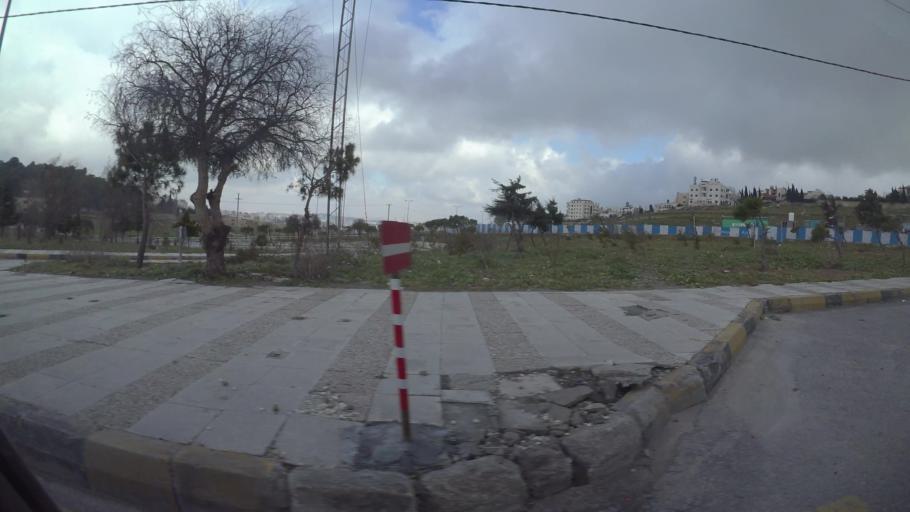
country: JO
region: Amman
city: Al Jubayhah
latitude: 32.0453
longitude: 35.8704
